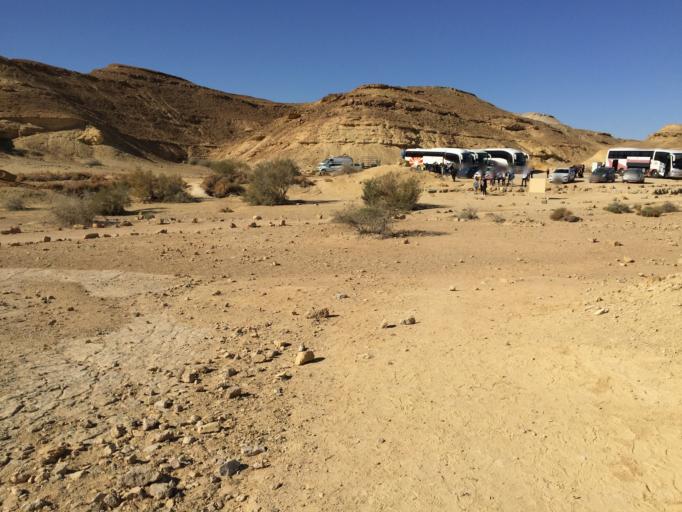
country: IL
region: Southern District
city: Mitzpe Ramon
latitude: 30.6053
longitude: 34.9385
